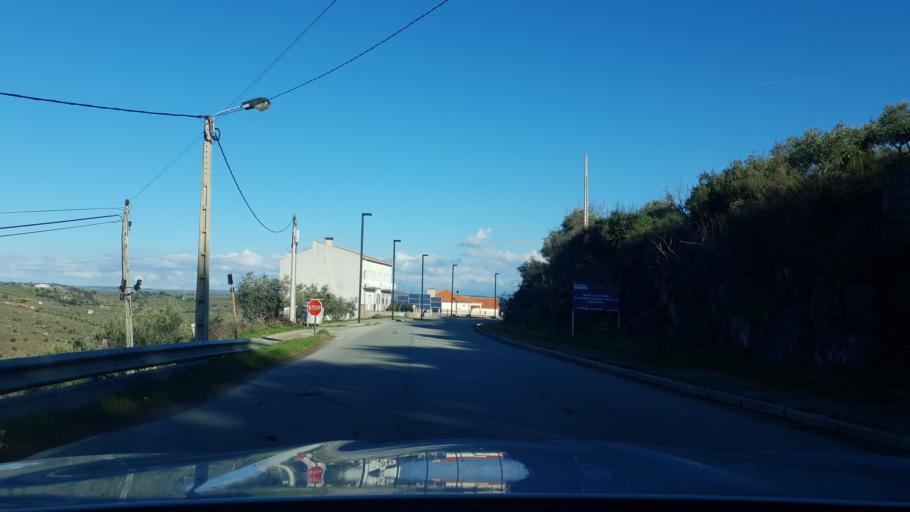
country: PT
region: Braganca
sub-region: Freixo de Espada A Cinta
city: Freixo de Espada a Cinta
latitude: 41.0951
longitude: -6.8151
